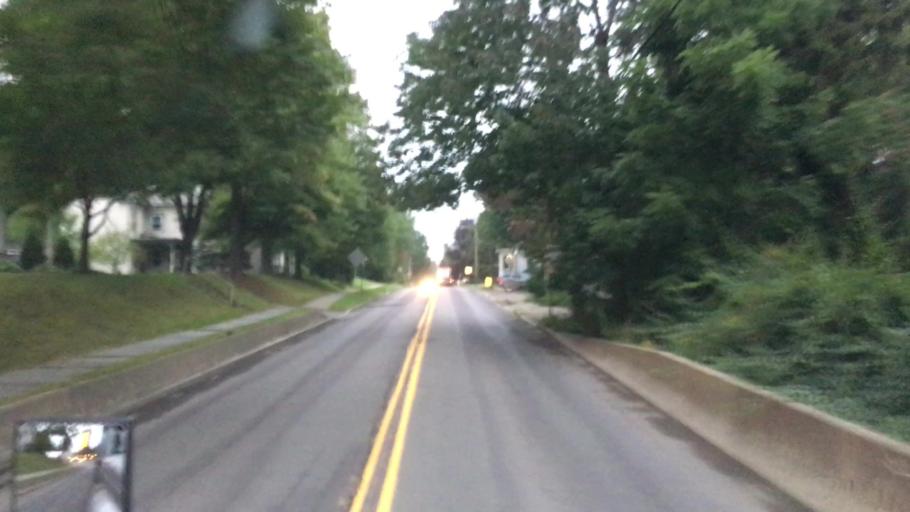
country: US
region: Pennsylvania
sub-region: Bradford County
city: Towanda
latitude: 41.7716
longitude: -76.4434
